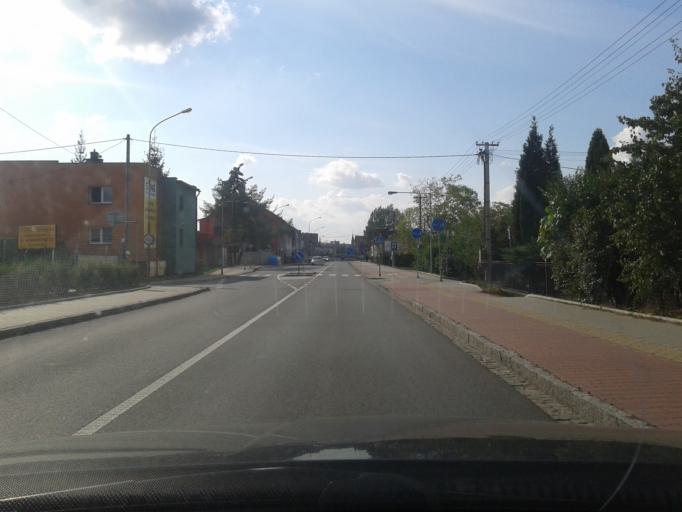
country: CZ
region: Moravskoslezsky
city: Bohumin
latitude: 49.9043
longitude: 18.3748
